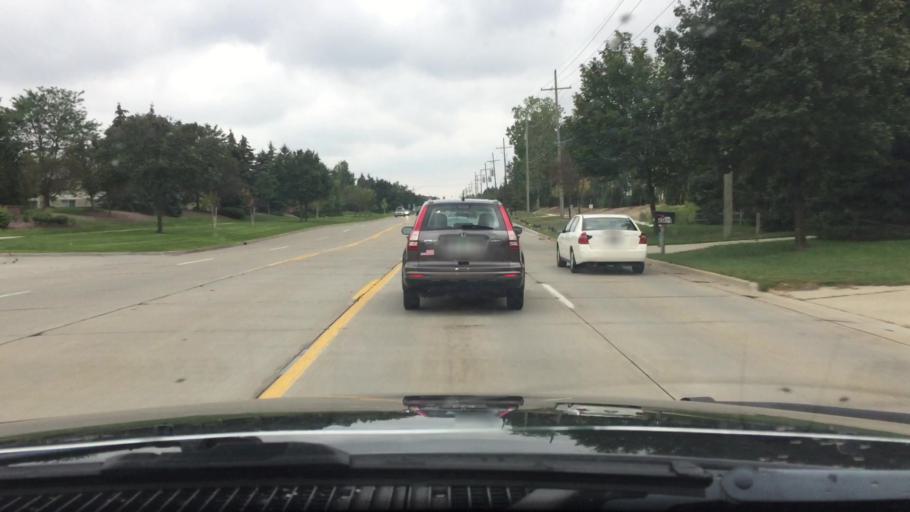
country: US
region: Michigan
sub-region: Macomb County
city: Utica
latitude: 42.6120
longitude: -83.0715
